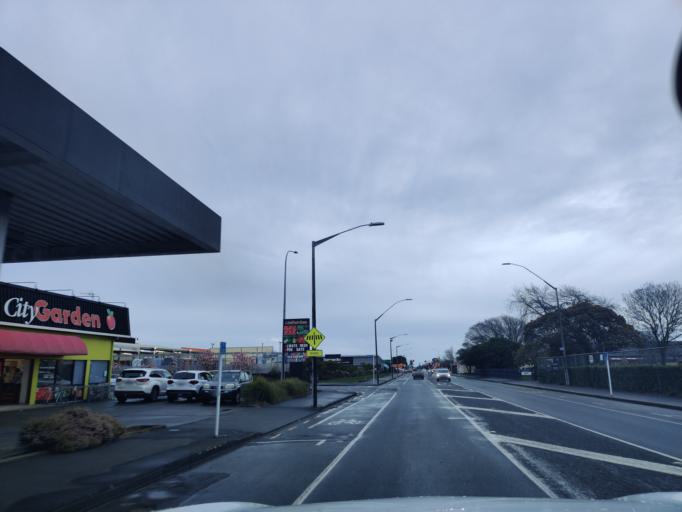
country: NZ
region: Manawatu-Wanganui
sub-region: Palmerston North City
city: Palmerston North
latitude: -40.3485
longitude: 175.6095
